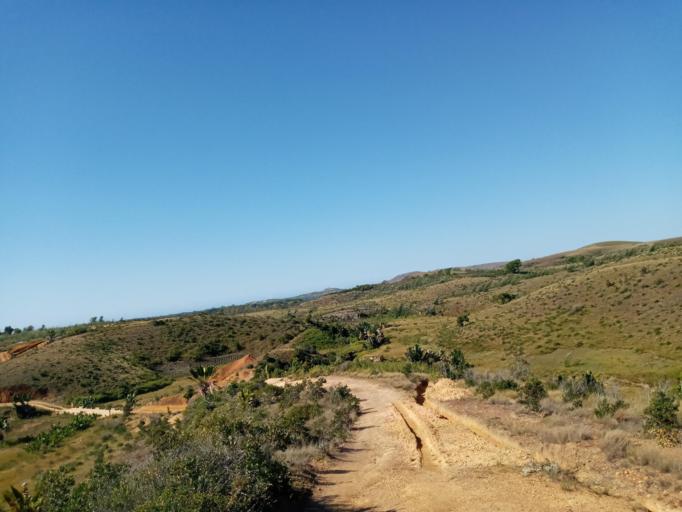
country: MG
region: Anosy
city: Fort Dauphin
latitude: -24.9134
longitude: 47.0859
